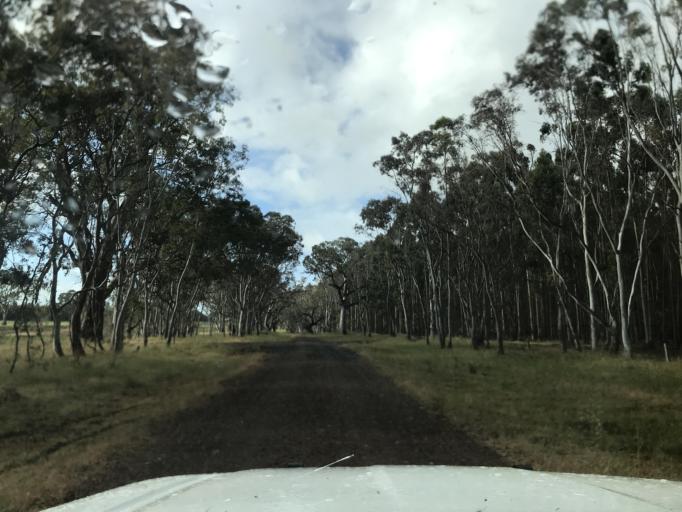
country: AU
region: South Australia
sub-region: Wattle Range
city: Penola
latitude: -37.2072
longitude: 141.2880
